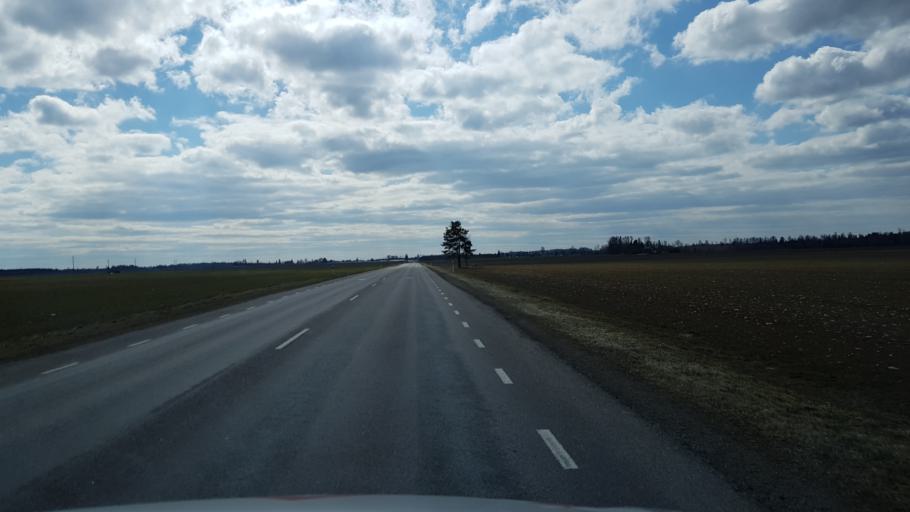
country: EE
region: Laeaene-Virumaa
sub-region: Vaeike-Maarja vald
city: Vaike-Maarja
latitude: 59.2047
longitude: 26.2690
